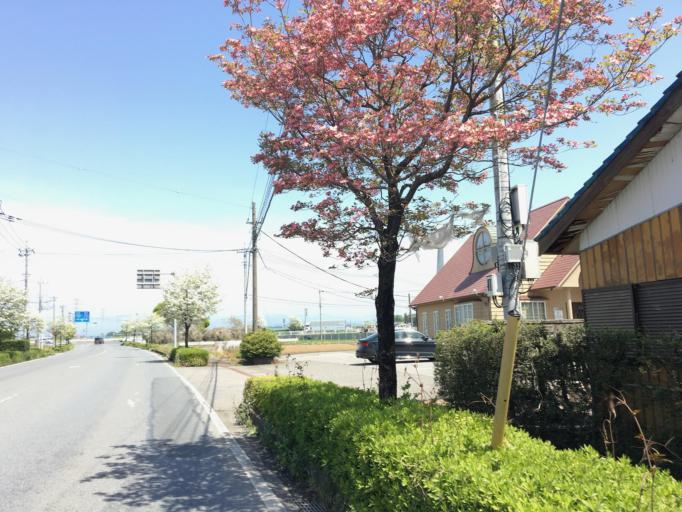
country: JP
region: Gunma
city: Sakai-nakajima
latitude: 36.2791
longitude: 139.2821
